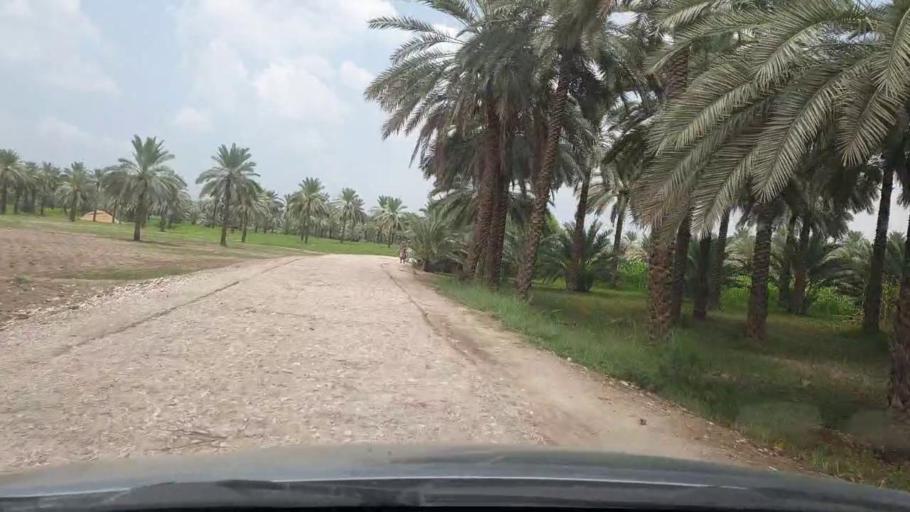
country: PK
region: Sindh
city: Kot Diji
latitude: 27.4142
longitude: 68.7494
